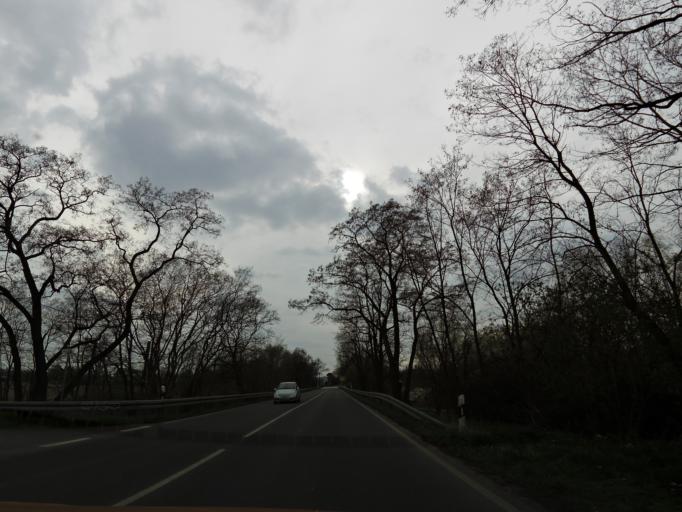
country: DE
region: Brandenburg
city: Frankfurt (Oder)
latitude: 52.3144
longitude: 14.4936
